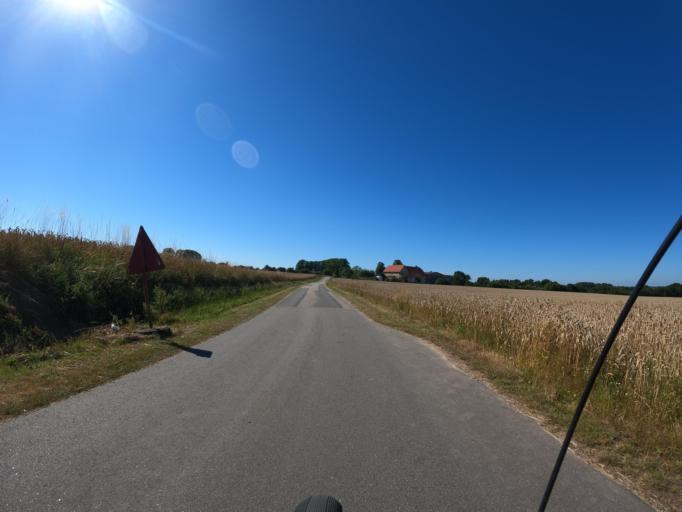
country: DE
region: Schleswig-Holstein
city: Steinberg
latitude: 54.7770
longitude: 9.7683
